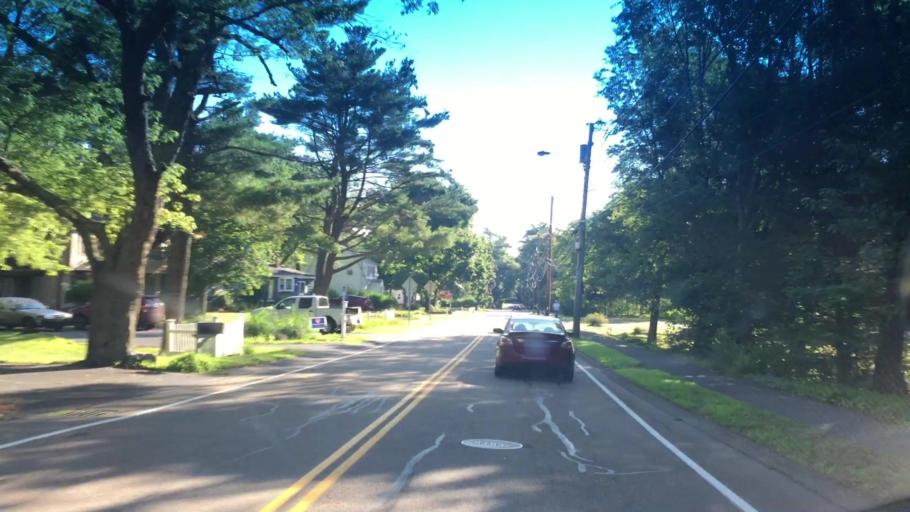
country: US
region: Massachusetts
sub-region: Norfolk County
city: Walpole
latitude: 42.1370
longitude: -71.2832
